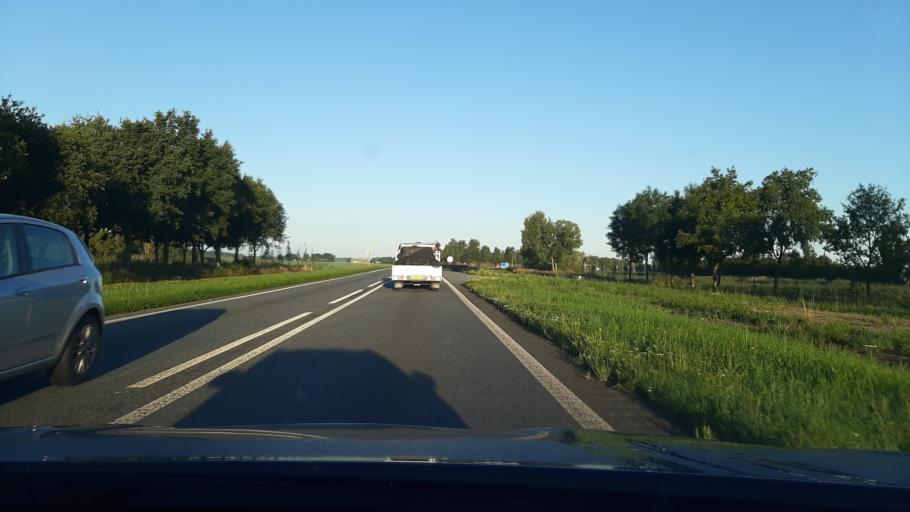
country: NL
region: Utrecht
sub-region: Gemeente Bunschoten
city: Spakenburg
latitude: 52.3097
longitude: 5.3575
